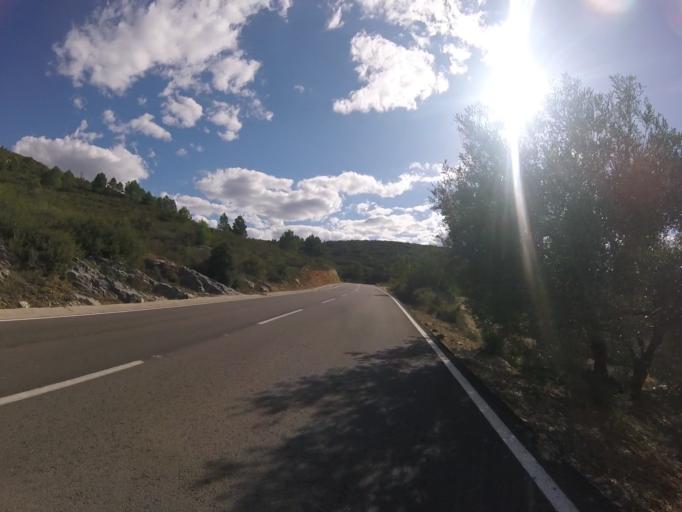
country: ES
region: Valencia
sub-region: Provincia de Castello
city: Cuevas de Vinroma
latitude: 40.2979
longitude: 0.1679
